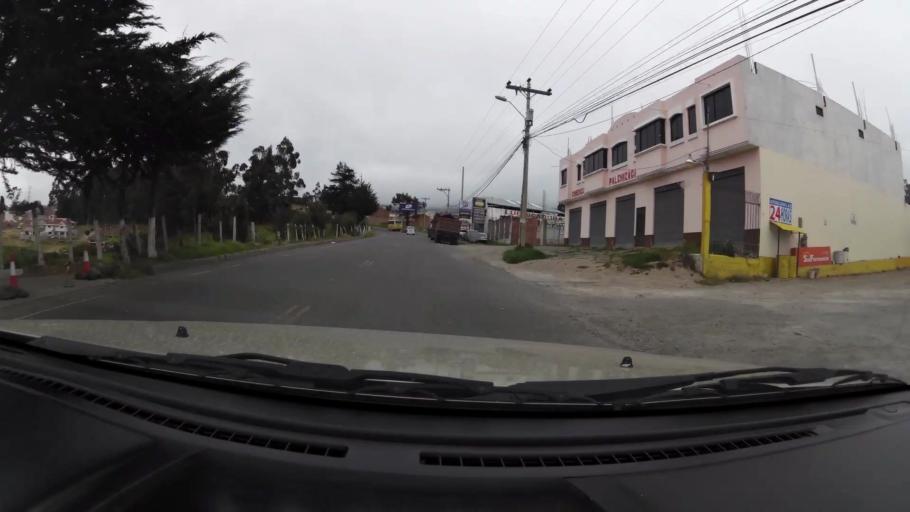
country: EC
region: Canar
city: Canar
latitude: -2.5176
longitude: -78.9271
